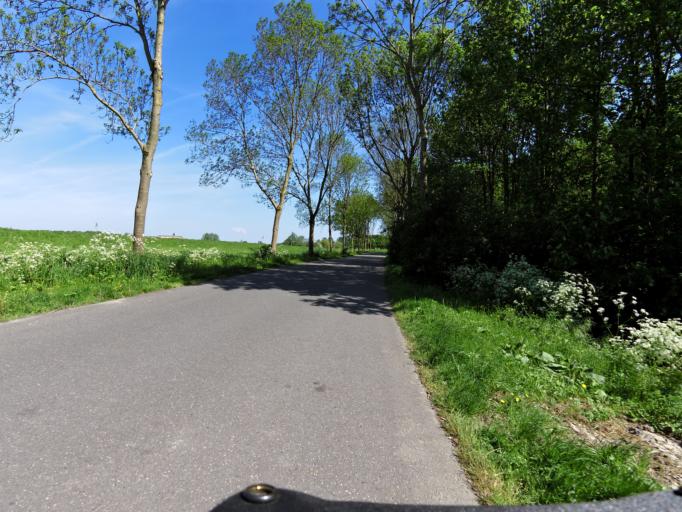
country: NL
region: South Holland
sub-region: Gemeente Barendrecht
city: Barendrecht
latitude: 51.8366
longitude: 4.5244
